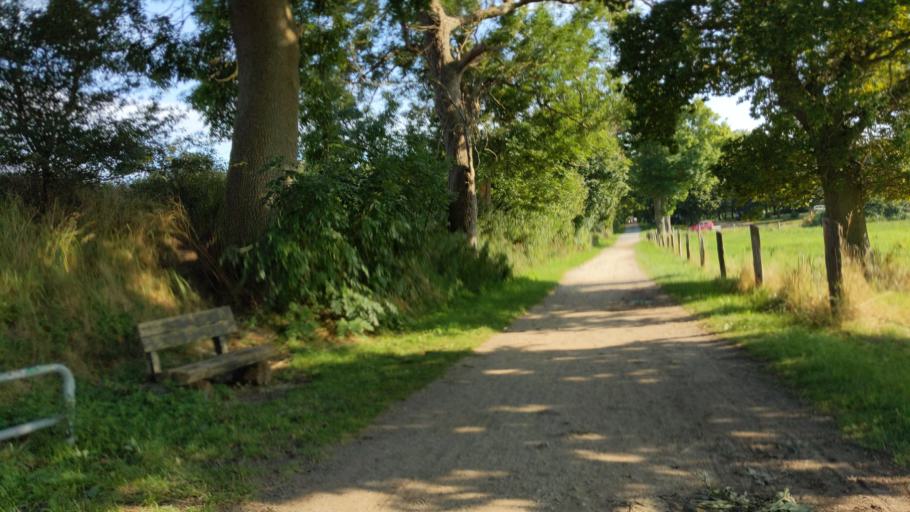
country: DE
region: Mecklenburg-Vorpommern
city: Kalkhorst
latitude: 54.0045
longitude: 11.0427
